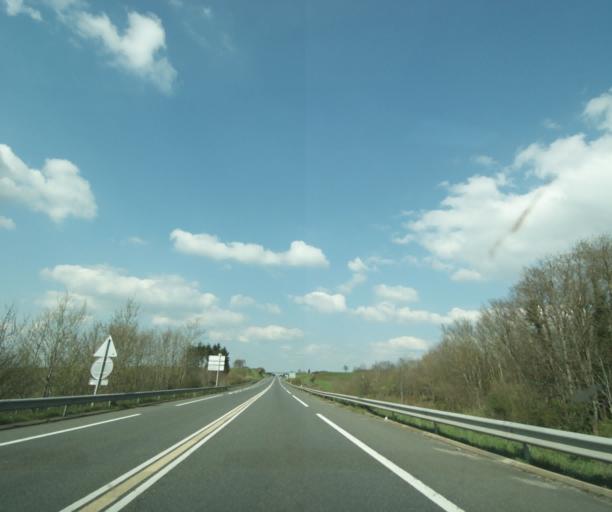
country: FR
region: Auvergne
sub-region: Departement de l'Allier
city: Montmarault
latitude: 46.3707
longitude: 3.0277
